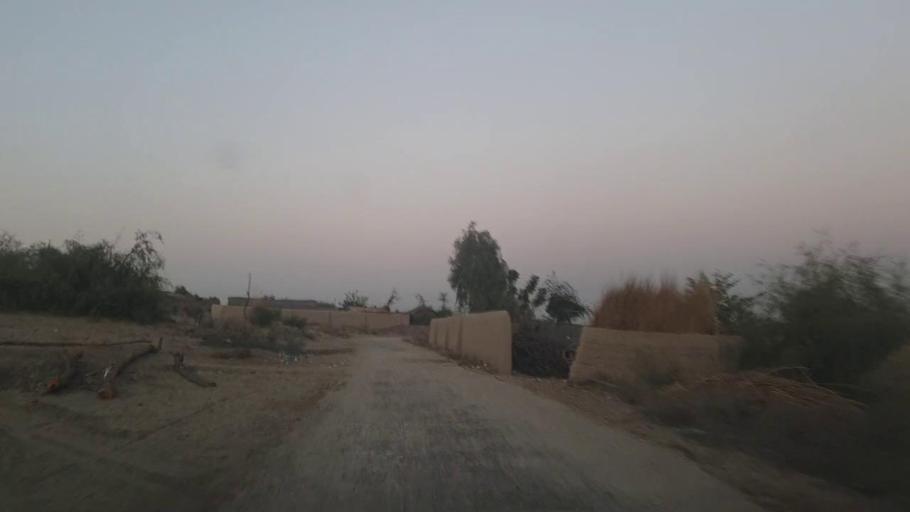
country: PK
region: Sindh
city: Jam Sahib
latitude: 26.3911
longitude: 68.8213
